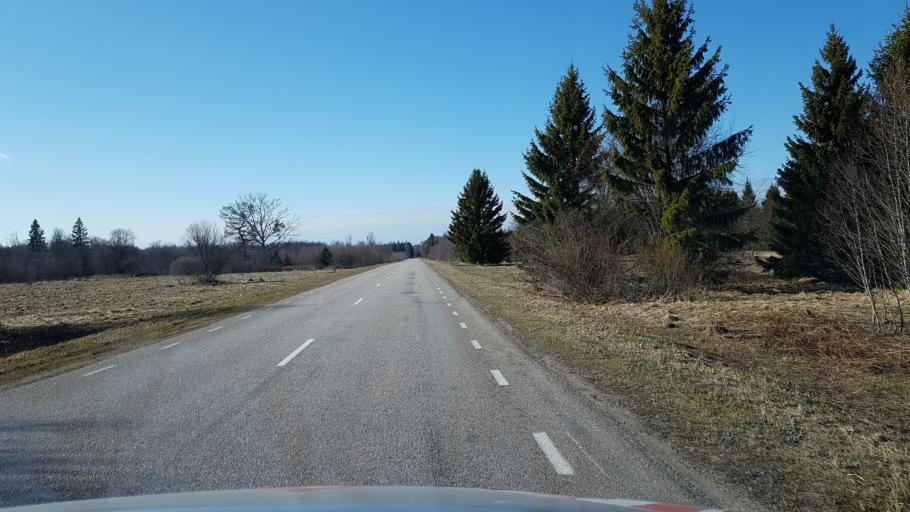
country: EE
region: Laeaene-Virumaa
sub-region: Haljala vald
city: Haljala
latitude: 59.5120
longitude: 26.1027
